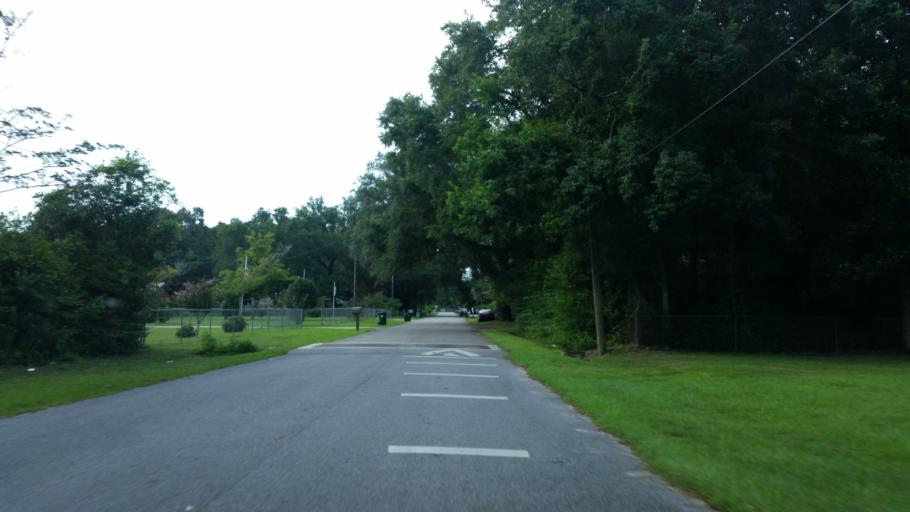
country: US
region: Florida
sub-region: Escambia County
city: Ferry Pass
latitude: 30.5140
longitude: -87.2085
